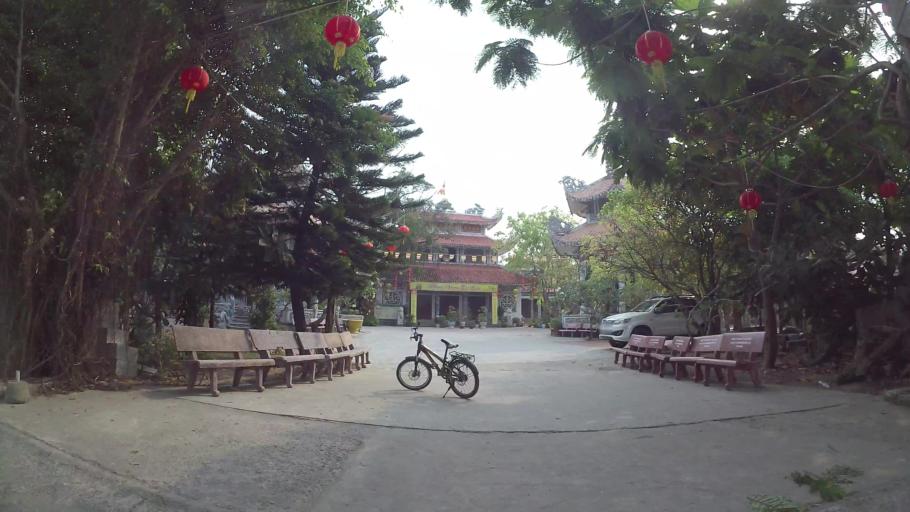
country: VN
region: Da Nang
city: Son Tra
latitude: 16.0894
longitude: 108.2466
